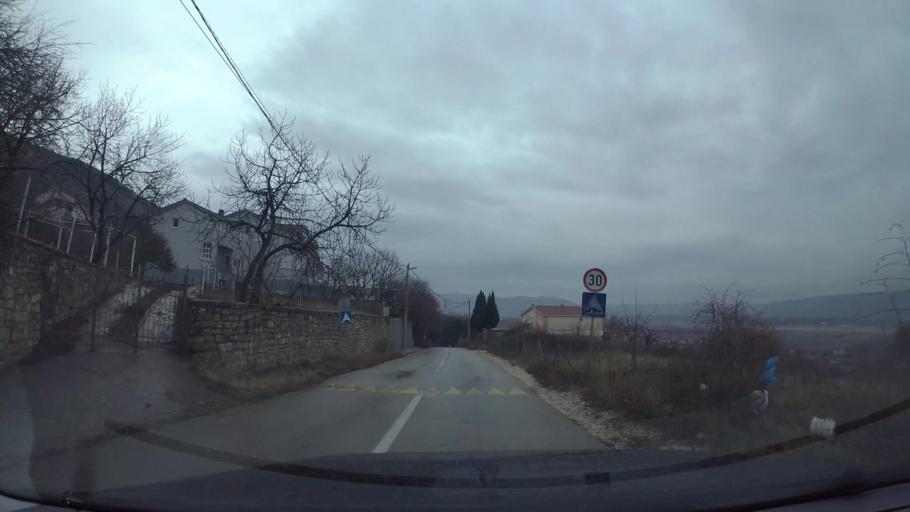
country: BA
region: Federation of Bosnia and Herzegovina
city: Blagaj
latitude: 43.2960
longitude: 17.8564
